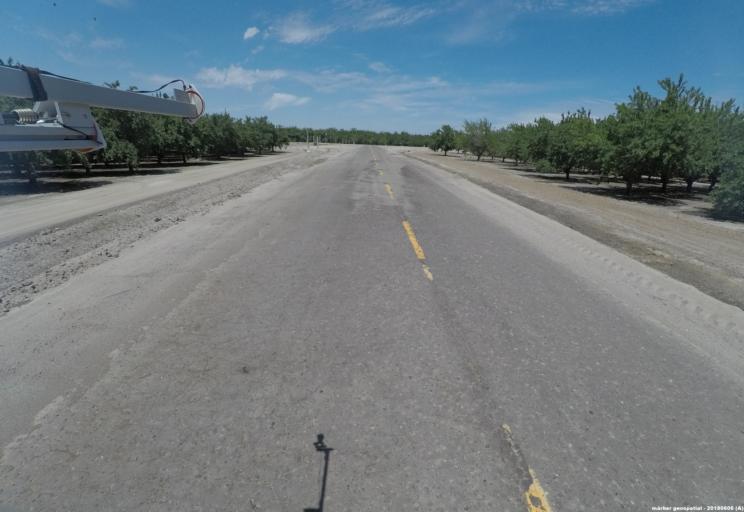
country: US
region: California
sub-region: Fresno County
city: Mendota
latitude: 36.8333
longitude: -120.3798
